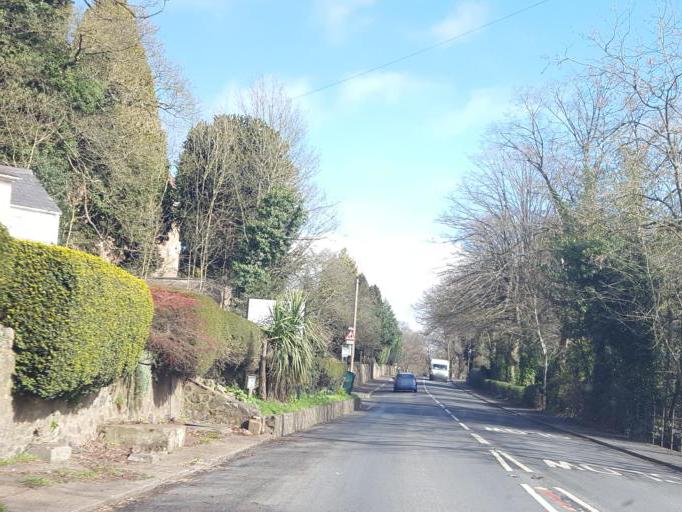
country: GB
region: England
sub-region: Worcestershire
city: Great Malvern
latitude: 52.0929
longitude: -2.3345
